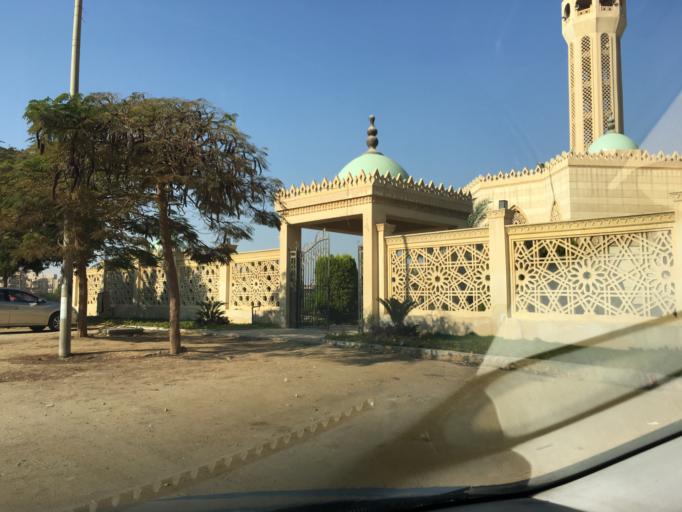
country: EG
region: Al Jizah
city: Madinat Sittah Uktubar
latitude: 29.9944
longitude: 30.9849
